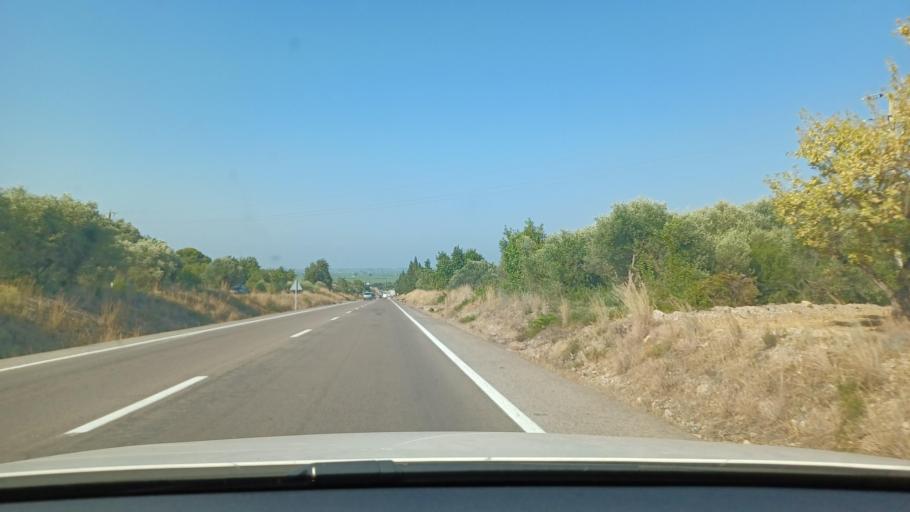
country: ES
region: Catalonia
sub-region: Provincia de Tarragona
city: Sant Carles de la Rapita
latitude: 40.6331
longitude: 0.5851
